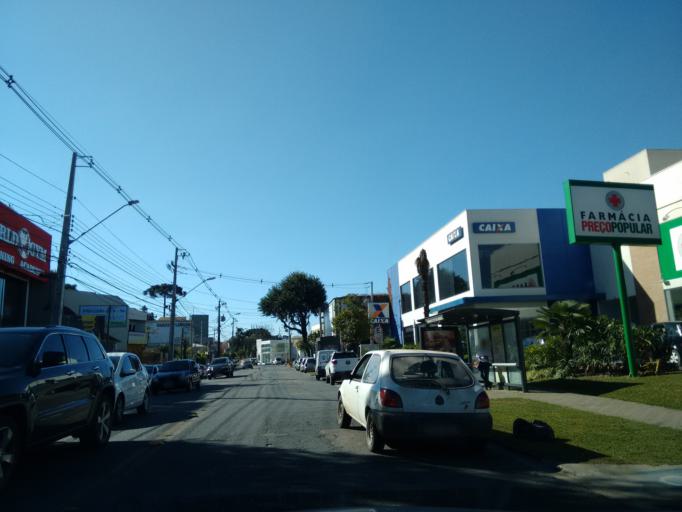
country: BR
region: Parana
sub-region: Curitiba
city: Curitiba
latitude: -25.4073
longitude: -49.2716
